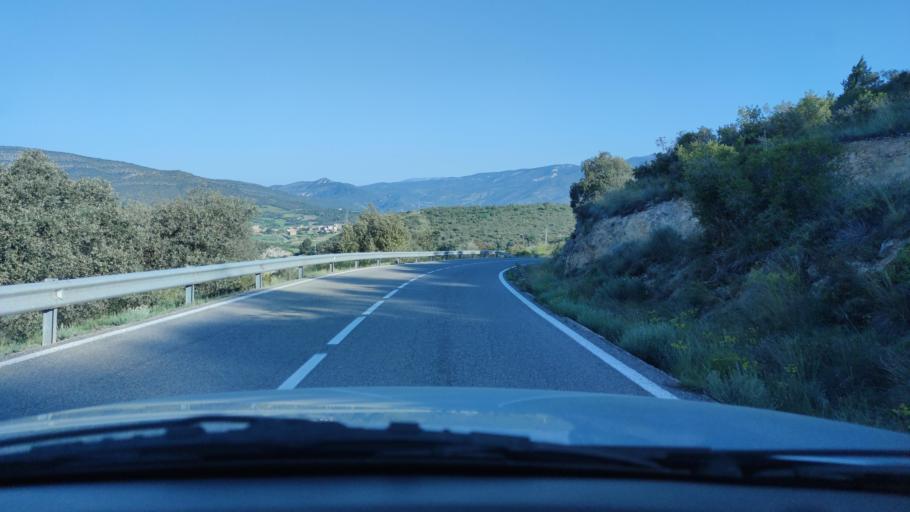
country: ES
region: Catalonia
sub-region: Provincia de Lleida
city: Artesa de Segre
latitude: 41.8817
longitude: 1.0066
